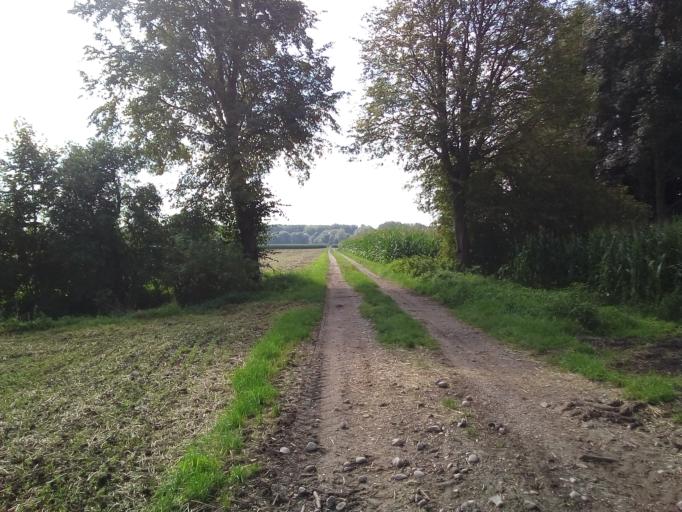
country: DE
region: Bavaria
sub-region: Upper Bavaria
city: Ismaning
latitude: 48.2172
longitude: 11.6987
